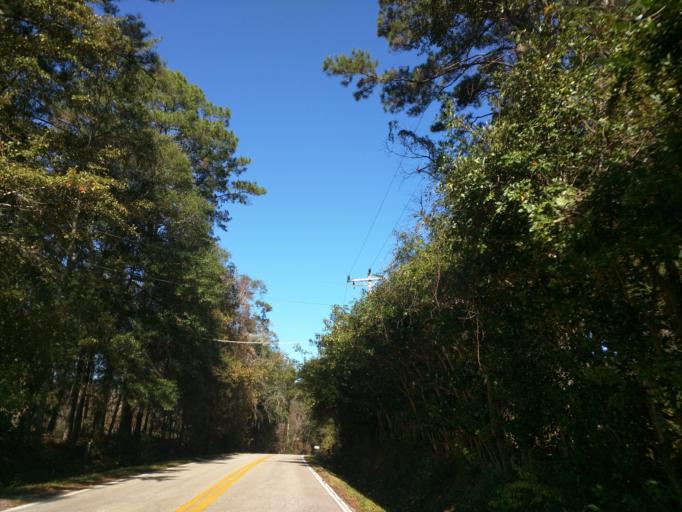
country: US
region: Florida
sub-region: Leon County
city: Tallahassee
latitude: 30.5049
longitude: -84.3216
